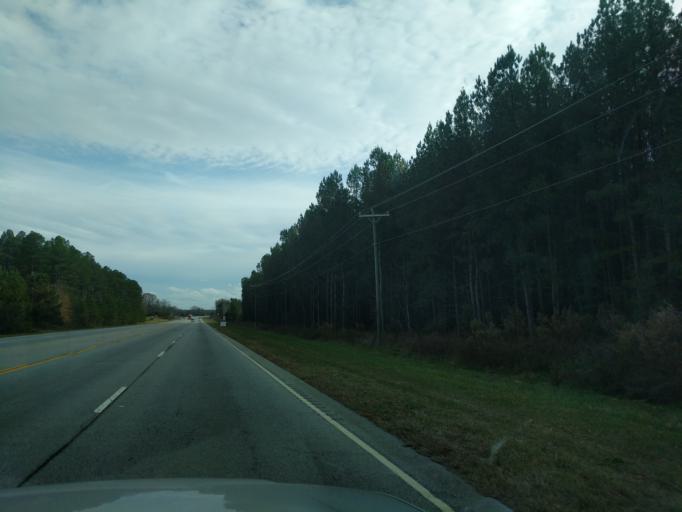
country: US
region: South Carolina
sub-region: Anderson County
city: Williamston
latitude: 34.6034
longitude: -82.3593
